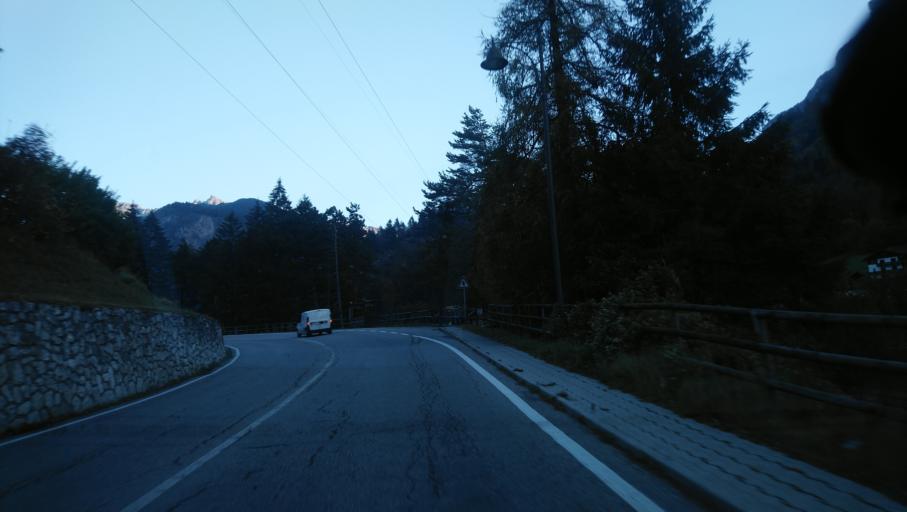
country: IT
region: Veneto
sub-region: Provincia di Belluno
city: Cencenighe Agordino
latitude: 46.3446
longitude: 11.9722
